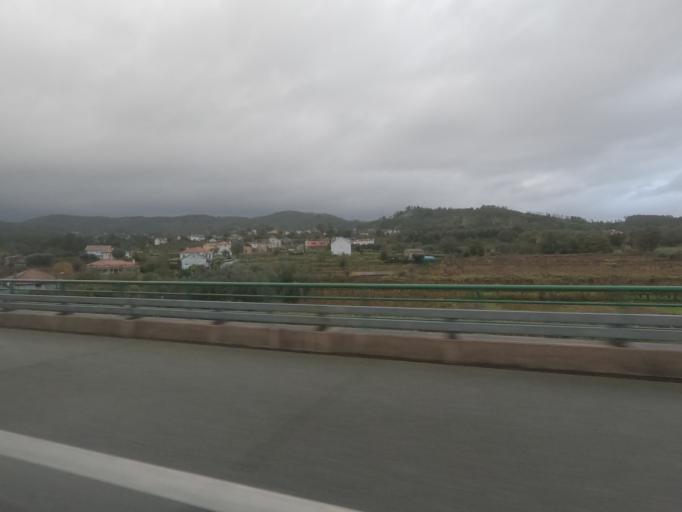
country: PT
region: Viana do Castelo
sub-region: Ponte de Lima
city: Ponte de Lima
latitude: 41.7933
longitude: -8.5781
